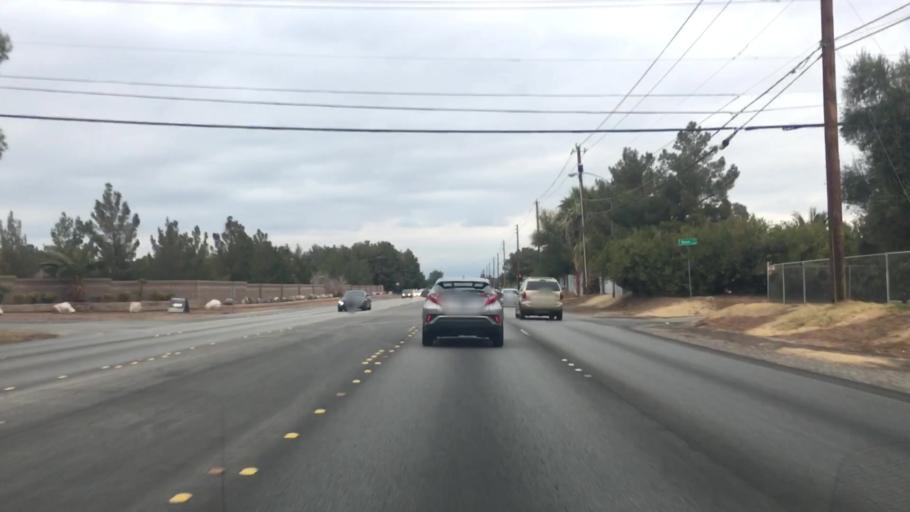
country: US
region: Nevada
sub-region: Clark County
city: Whitney
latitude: 36.0640
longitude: -115.1005
